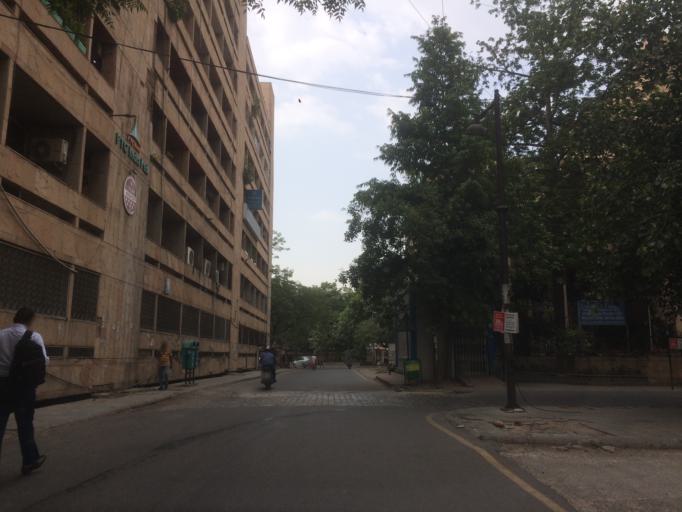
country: IN
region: NCT
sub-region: New Delhi
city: New Delhi
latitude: 28.5682
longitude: 77.1857
